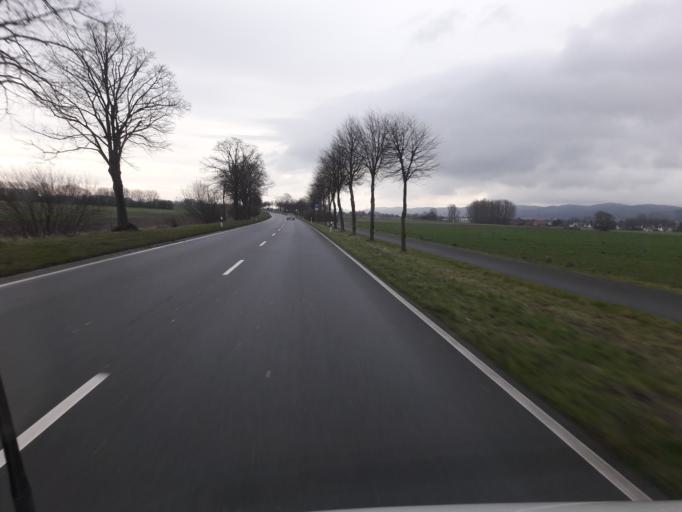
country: DE
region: North Rhine-Westphalia
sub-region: Regierungsbezirk Detmold
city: Hille
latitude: 52.3008
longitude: 8.7434
